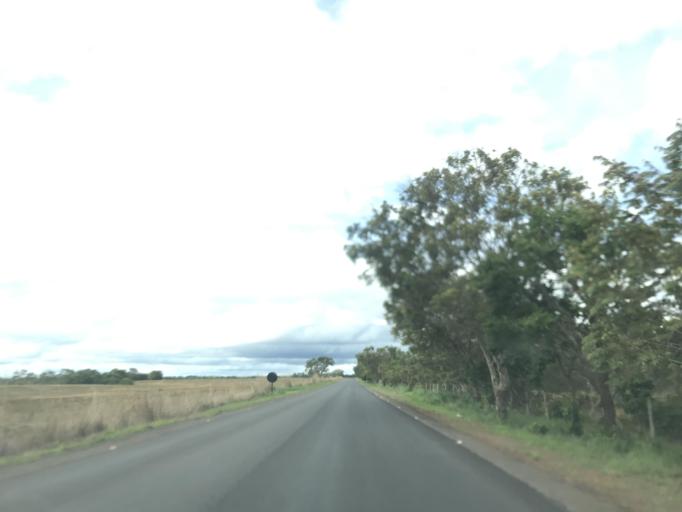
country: BR
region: Goias
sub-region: Bela Vista De Goias
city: Bela Vista de Goias
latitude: -16.9950
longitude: -48.6700
